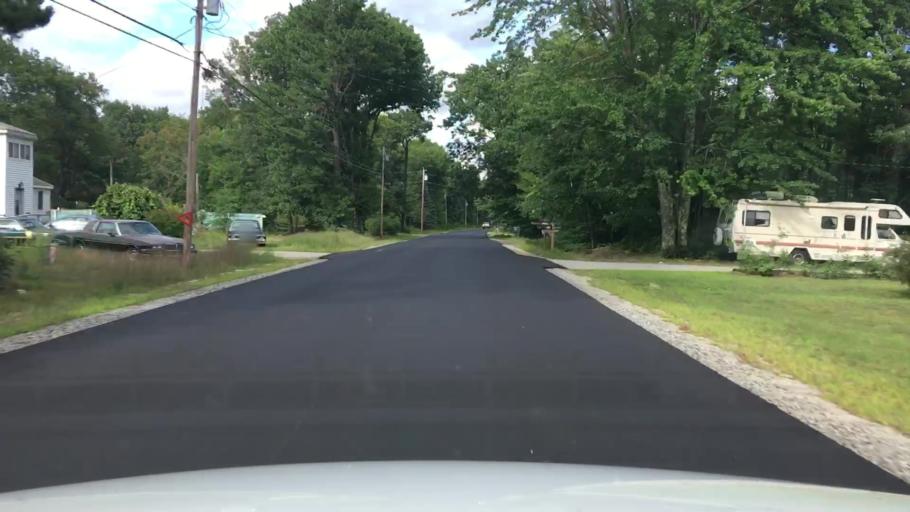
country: US
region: Maine
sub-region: York County
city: West Kennebunk
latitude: 43.4309
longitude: -70.6452
